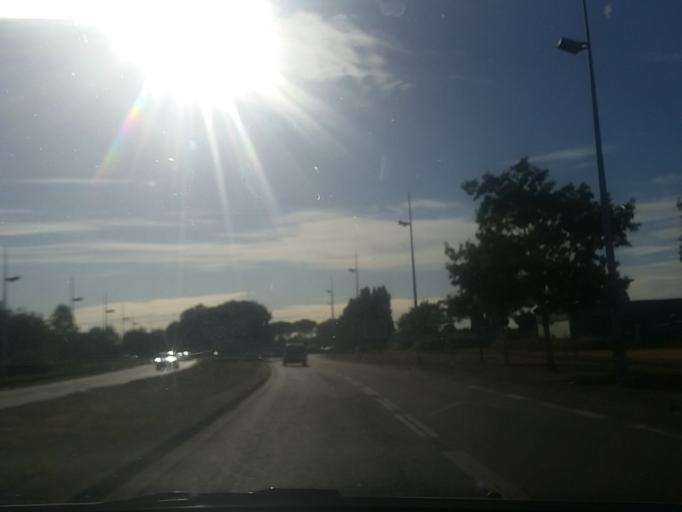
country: FR
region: Pays de la Loire
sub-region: Departement de la Loire-Atlantique
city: Reze
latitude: 47.1925
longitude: -1.5604
